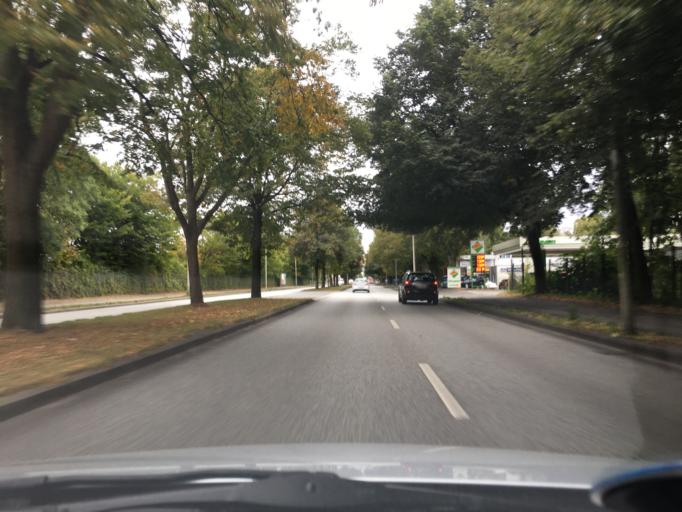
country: DE
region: Schleswig-Holstein
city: Kronshagen
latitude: 54.3379
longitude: 10.1060
